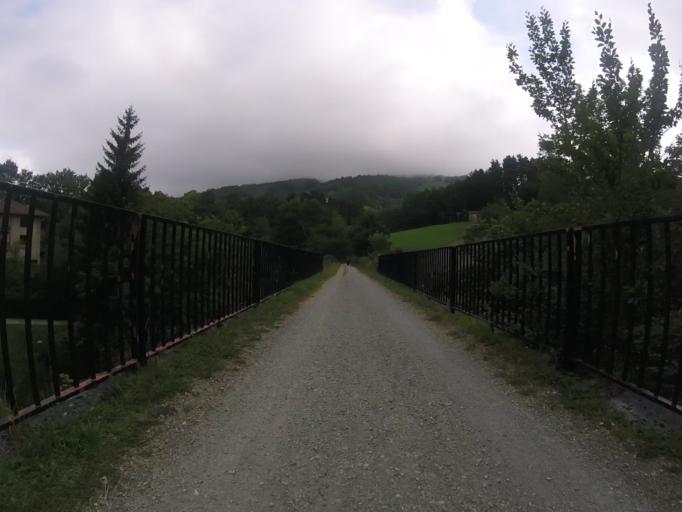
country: ES
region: Navarre
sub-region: Provincia de Navarra
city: Leitza
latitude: 43.0853
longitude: -1.9022
